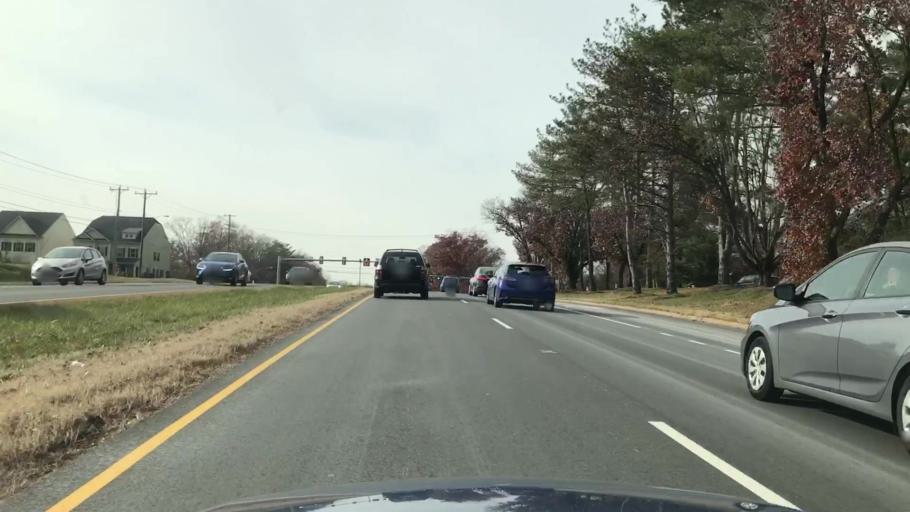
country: US
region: Virginia
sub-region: Fairfax County
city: Mantua
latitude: 38.8652
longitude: -77.2569
